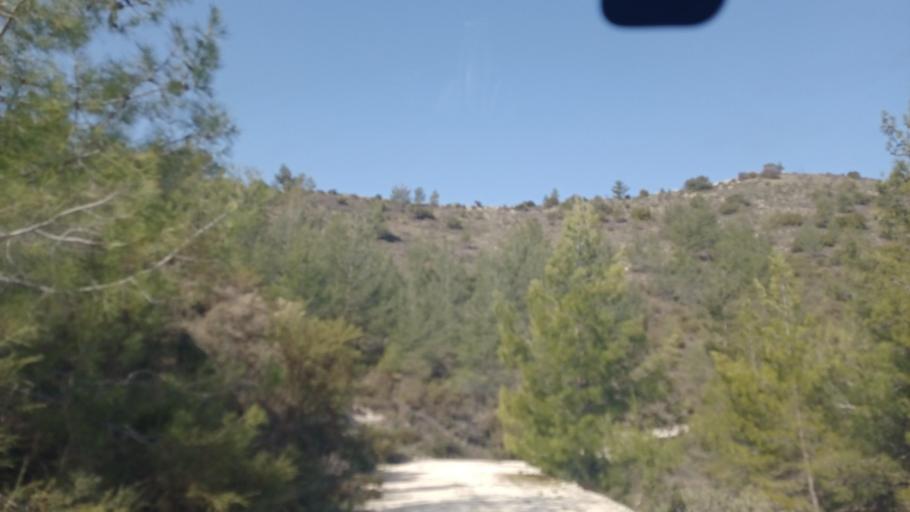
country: CY
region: Limassol
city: Pachna
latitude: 34.8849
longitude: 32.7310
